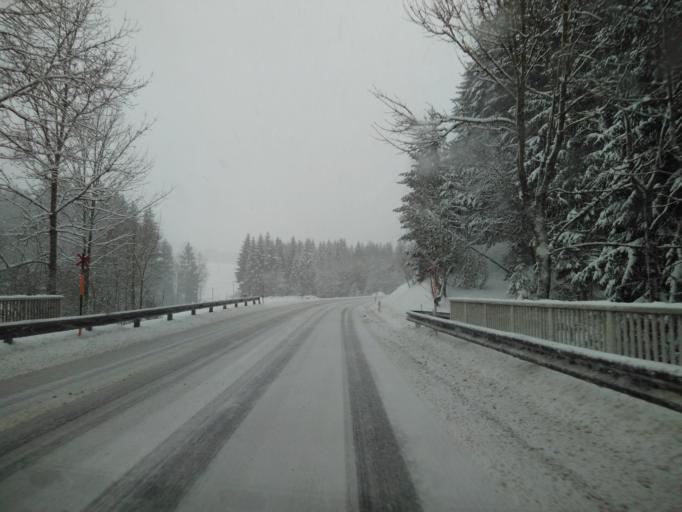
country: AT
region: Upper Austria
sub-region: Politischer Bezirk Urfahr-Umgebung
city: Zwettl an der Rodl
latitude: 48.4784
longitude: 14.2900
